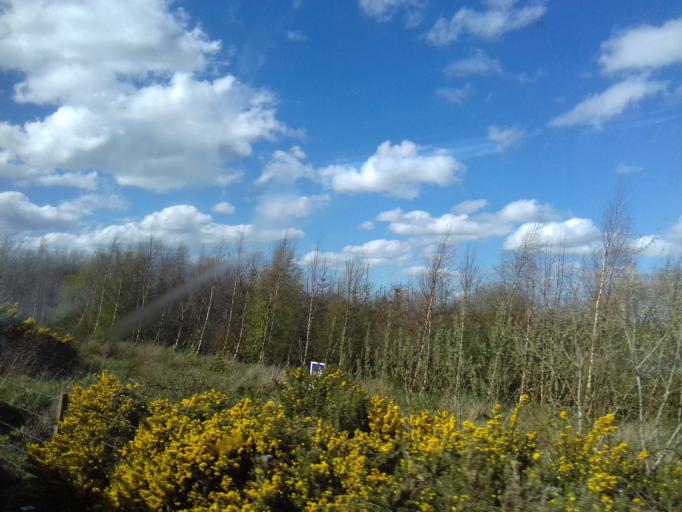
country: IE
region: Munster
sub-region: County Cork
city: Kanturk
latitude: 52.1288
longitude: -8.8285
